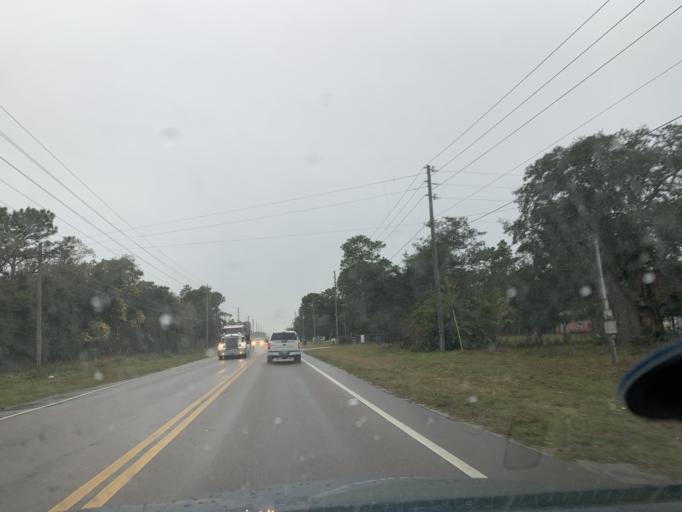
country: US
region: Florida
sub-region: Hernando County
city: Masaryktown
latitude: 28.4337
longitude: -82.5003
